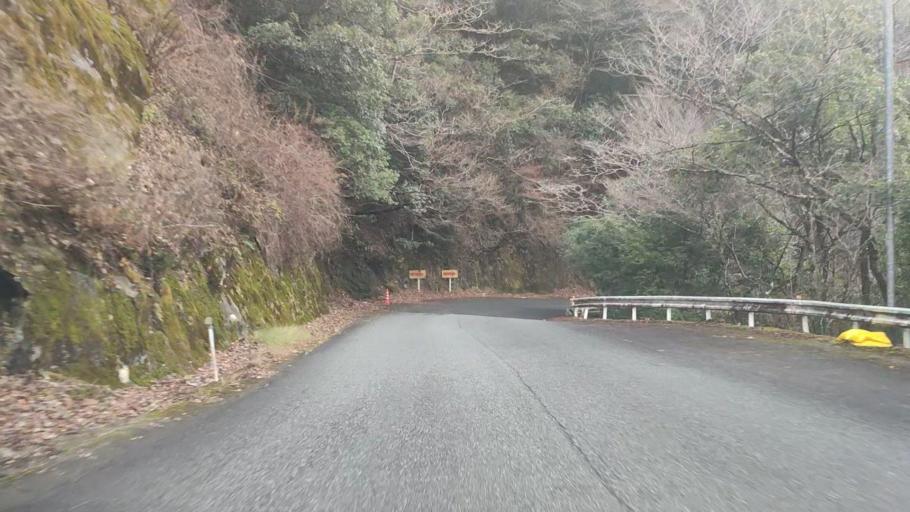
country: JP
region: Kumamoto
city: Matsubase
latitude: 32.4871
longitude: 130.8987
